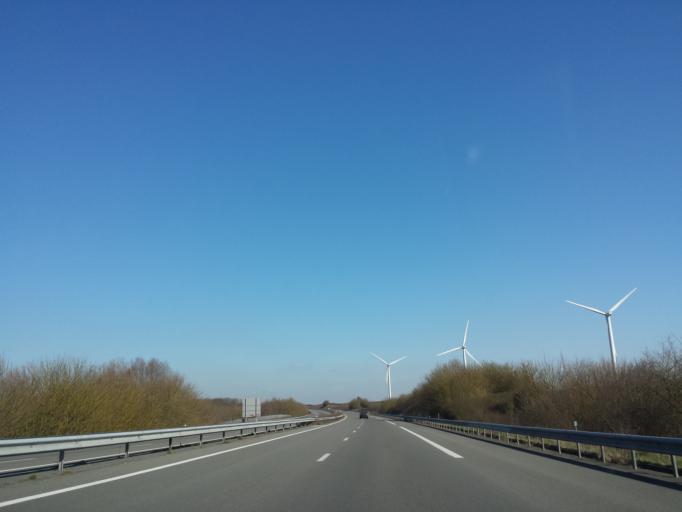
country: FR
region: Picardie
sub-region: Departement de l'Oise
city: Breteuil
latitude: 49.6904
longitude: 2.2283
